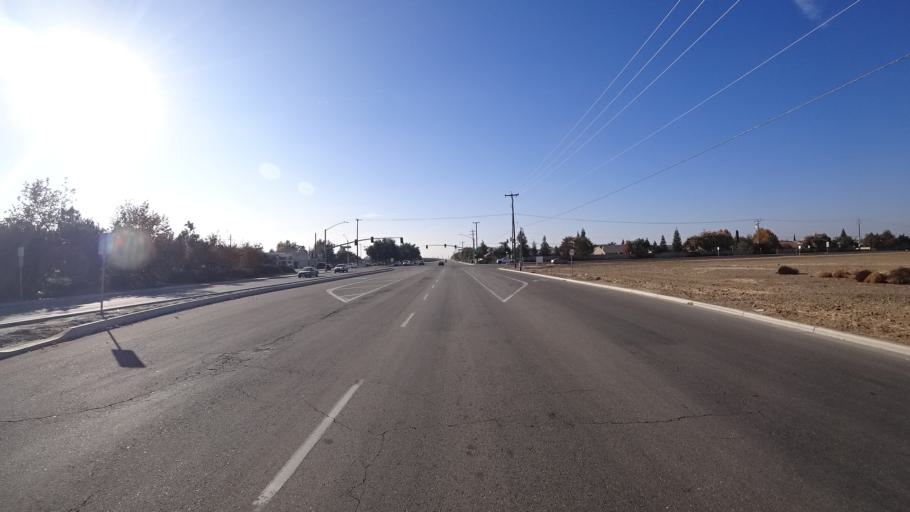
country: US
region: California
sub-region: Kern County
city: Greenacres
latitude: 35.2963
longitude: -119.1271
